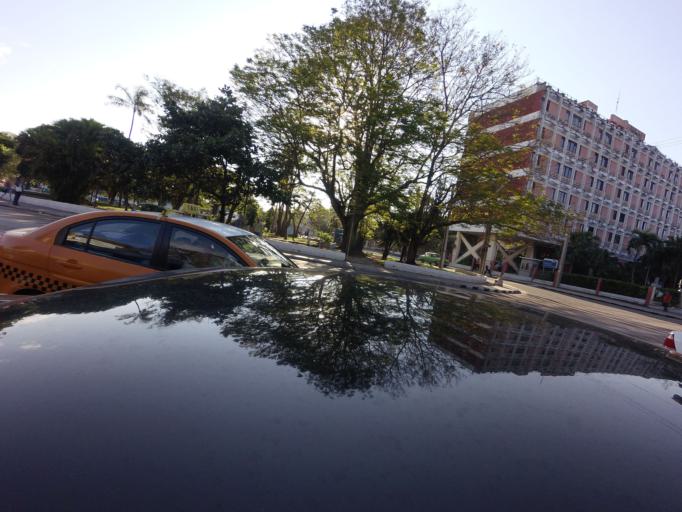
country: CU
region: La Habana
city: Cerro
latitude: 23.0927
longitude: -82.4226
